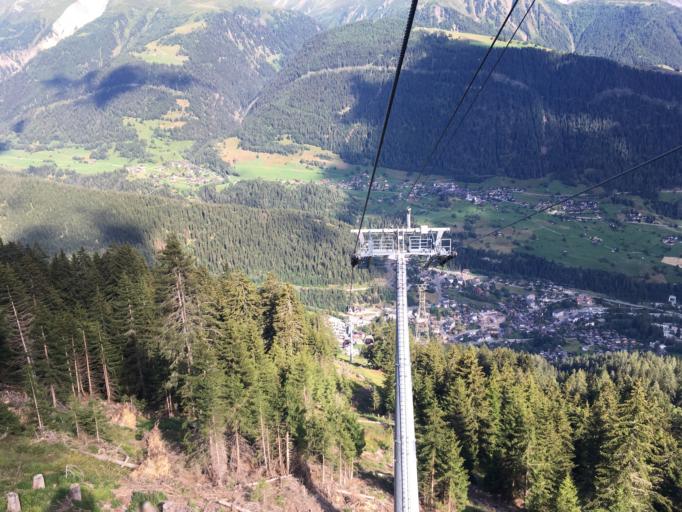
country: CH
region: Valais
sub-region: Goms District
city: Fiesch
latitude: 46.4099
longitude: 8.1177
